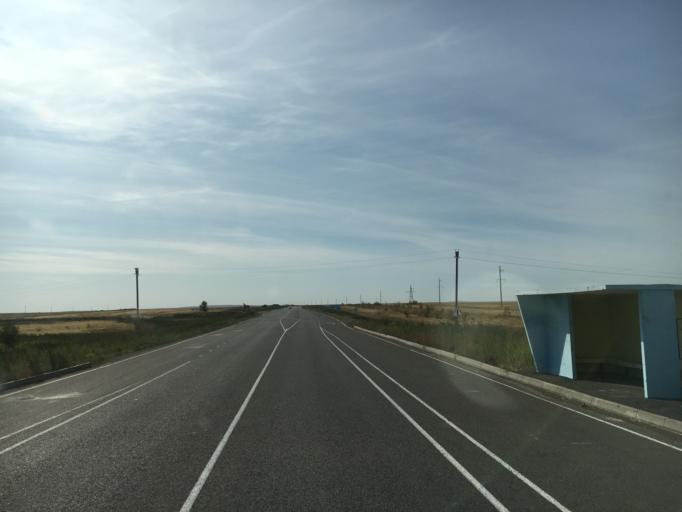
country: KZ
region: Batys Qazaqstan
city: Peremetnoe
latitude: 51.1202
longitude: 50.7421
